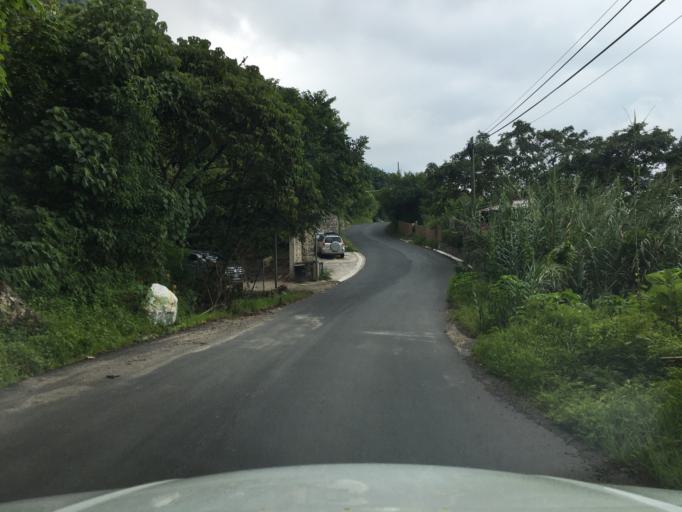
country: GT
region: Solola
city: Panajachel
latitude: 14.7321
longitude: -91.1426
